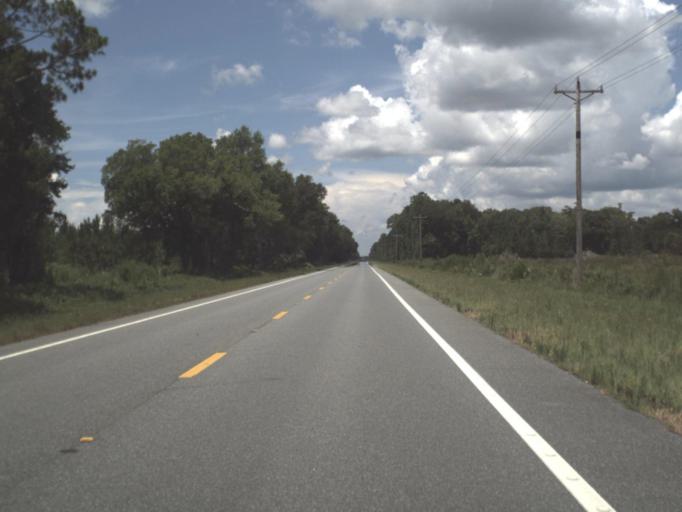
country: US
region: Florida
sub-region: Taylor County
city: Perry
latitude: 30.1428
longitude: -83.8078
